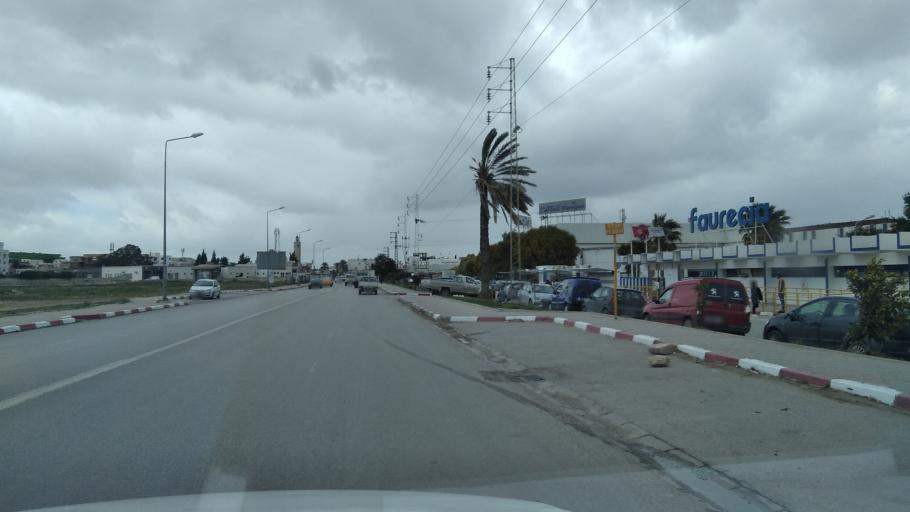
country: TN
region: Bin 'Arus
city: Ben Arous
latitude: 36.7489
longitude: 10.2286
